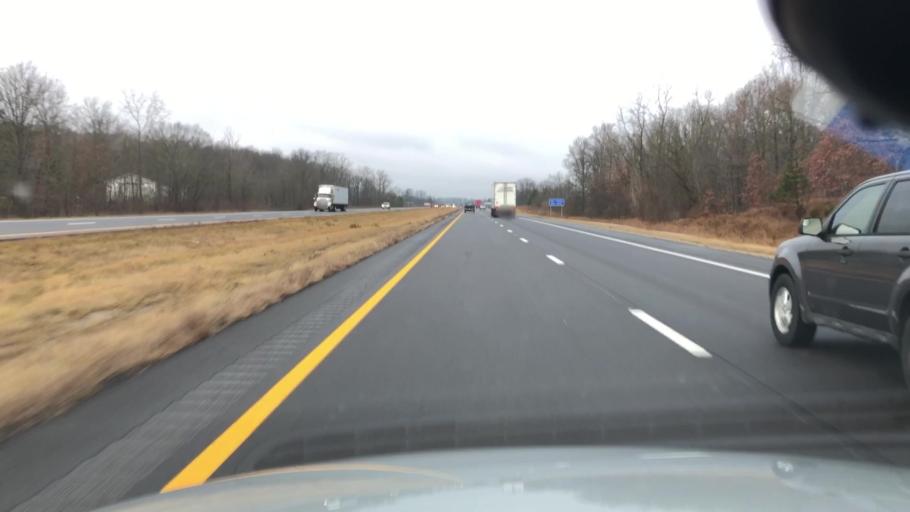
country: US
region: Ohio
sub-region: Champaign County
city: North Lewisburg
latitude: 40.2633
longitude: -83.4788
